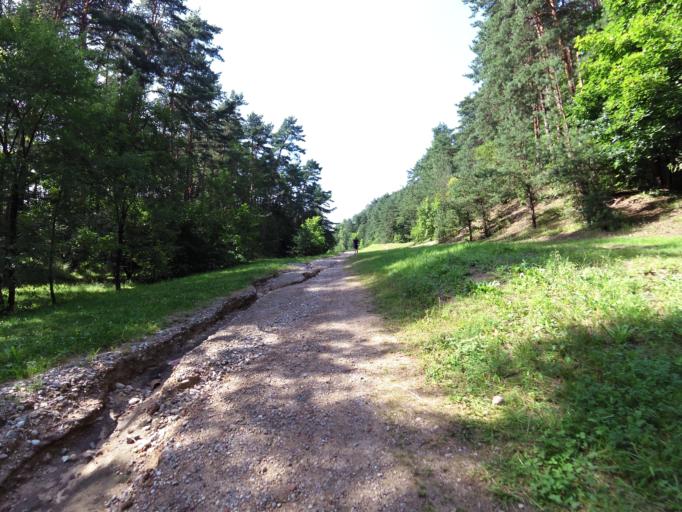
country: LT
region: Vilnius County
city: Seskine
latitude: 54.7002
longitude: 25.2399
